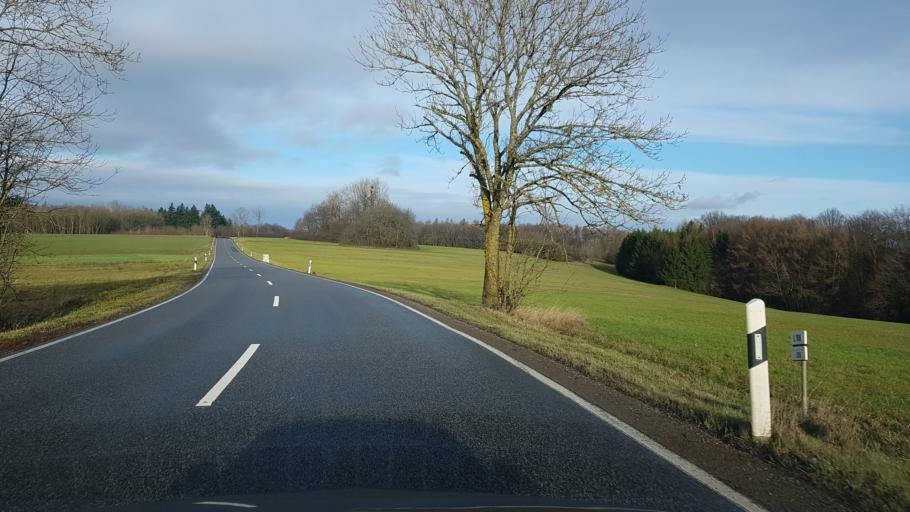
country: DE
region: Saarland
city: Sankt Ingbert
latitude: 49.2406
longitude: 7.1277
